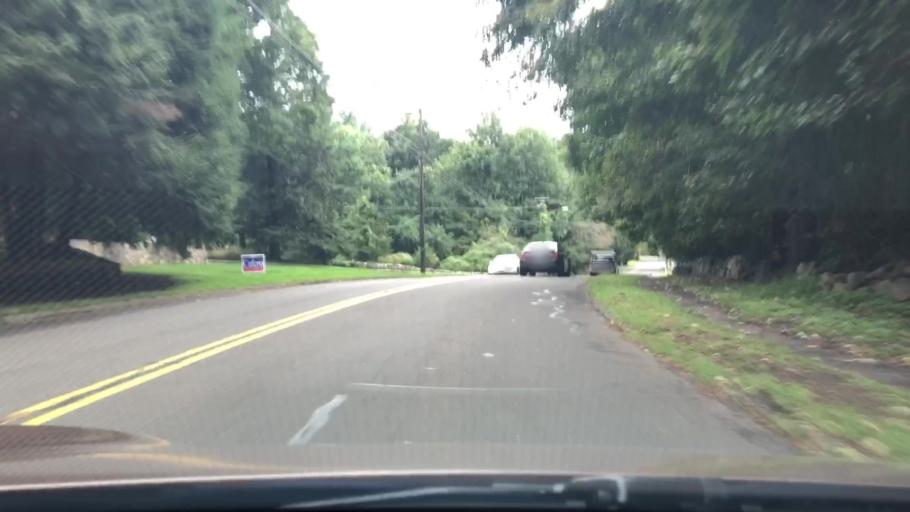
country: US
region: Connecticut
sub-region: Fairfield County
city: Norwalk
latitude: 41.1224
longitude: -73.4519
